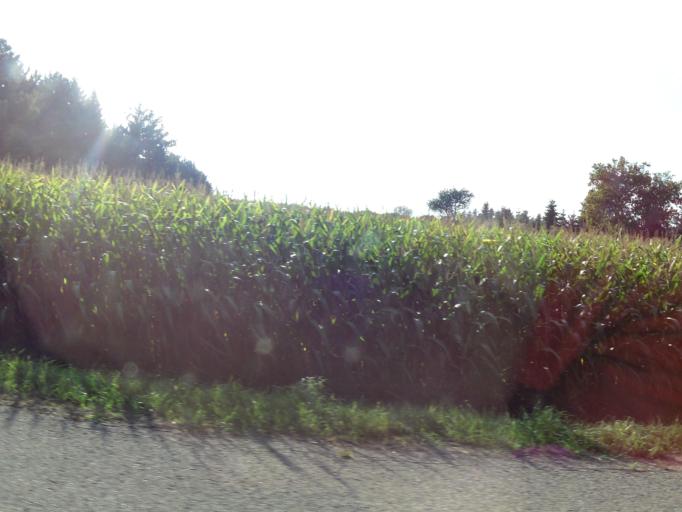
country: US
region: Minnesota
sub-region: Washington County
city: Oak Park Heights
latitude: 44.9888
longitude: -92.8224
